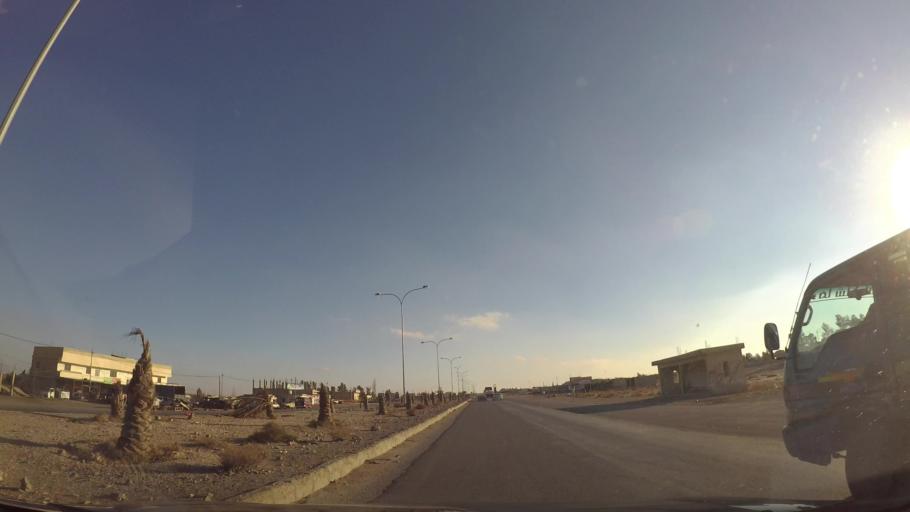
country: JO
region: Tafielah
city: Busayra
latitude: 30.5946
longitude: 35.8034
